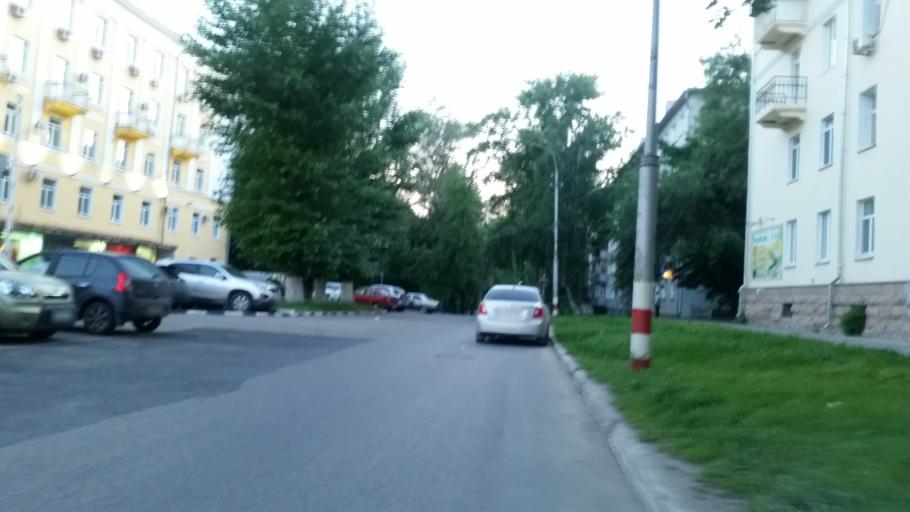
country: RU
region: Ulyanovsk
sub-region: Ulyanovskiy Rayon
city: Ulyanovsk
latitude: 54.3102
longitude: 48.3958
